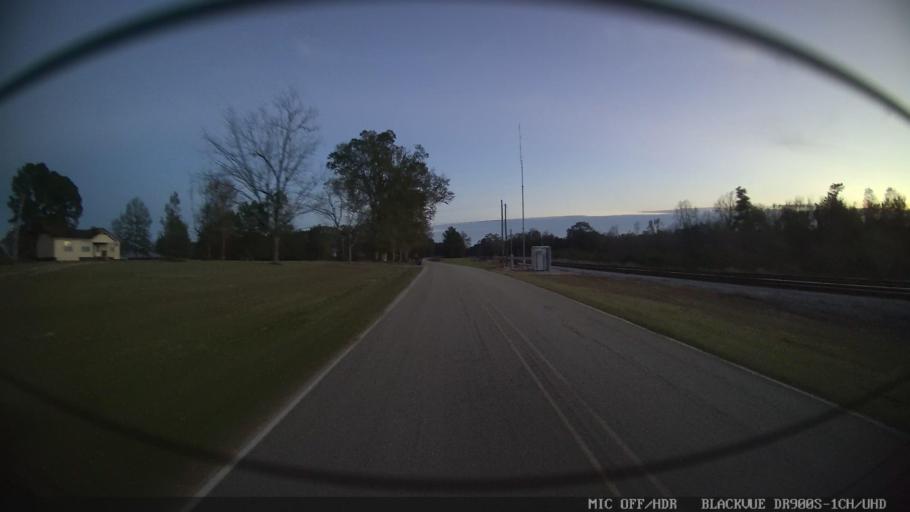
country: US
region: Mississippi
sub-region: Perry County
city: New Augusta
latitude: 31.1624
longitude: -89.2130
